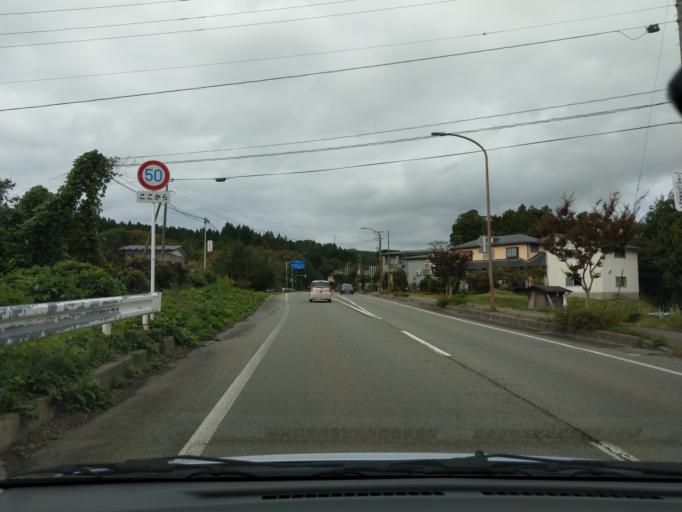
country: JP
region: Akita
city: Akita Shi
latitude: 39.6700
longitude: 140.0843
